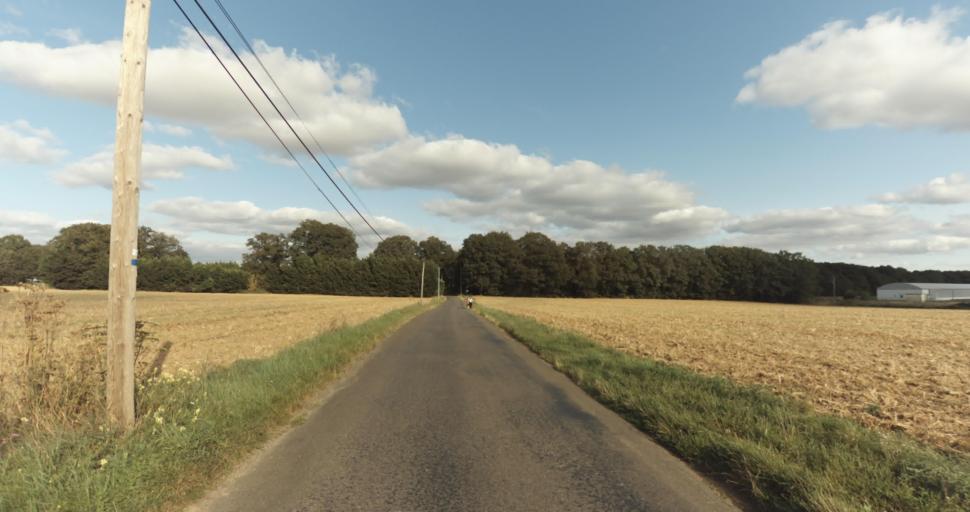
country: FR
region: Haute-Normandie
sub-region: Departement de l'Eure
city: Marcilly-sur-Eure
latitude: 48.9065
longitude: 1.2893
